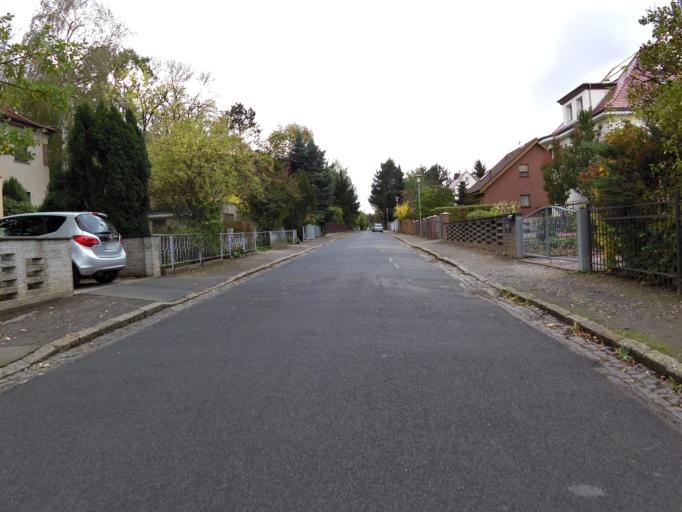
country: DE
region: Saxony
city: Grossposna
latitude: 51.2942
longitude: 12.4460
